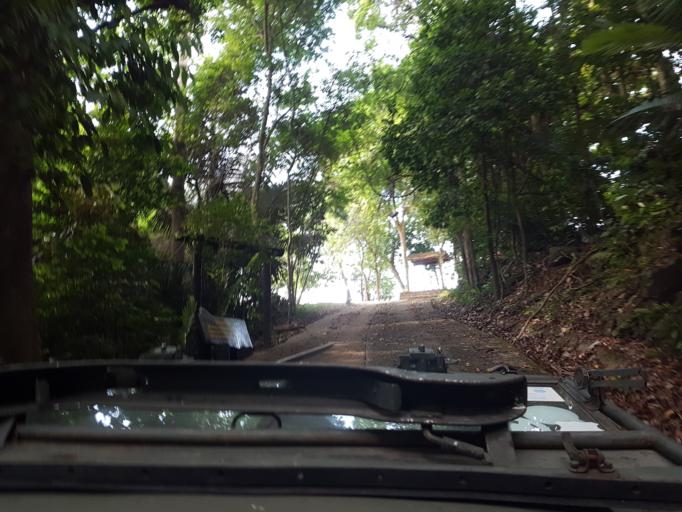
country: TH
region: Pattani
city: Khok Pho
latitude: 6.6556
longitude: 101.1005
